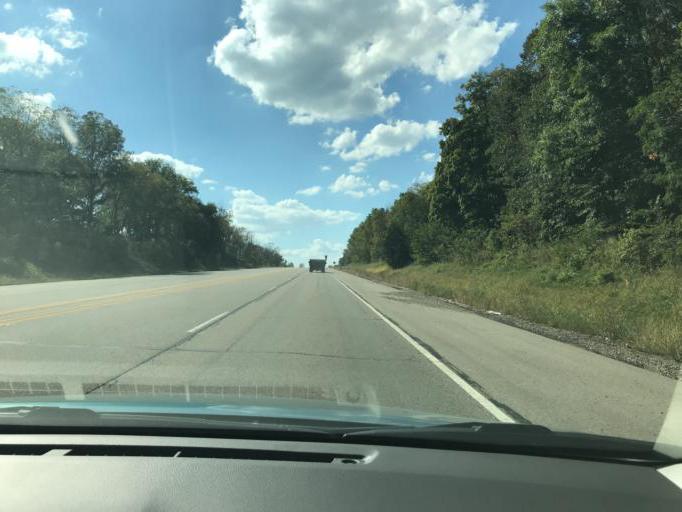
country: US
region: Wisconsin
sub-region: Walworth County
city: Lake Geneva
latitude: 42.5901
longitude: -88.4556
